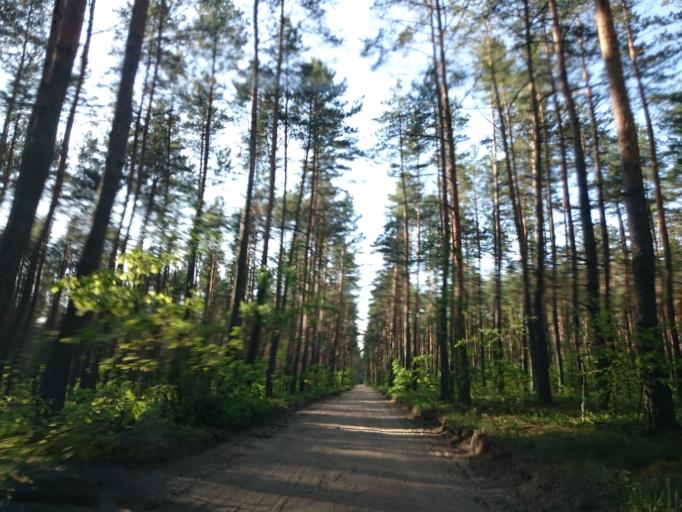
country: LV
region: Stopini
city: Ulbroka
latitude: 56.9492
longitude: 24.3511
